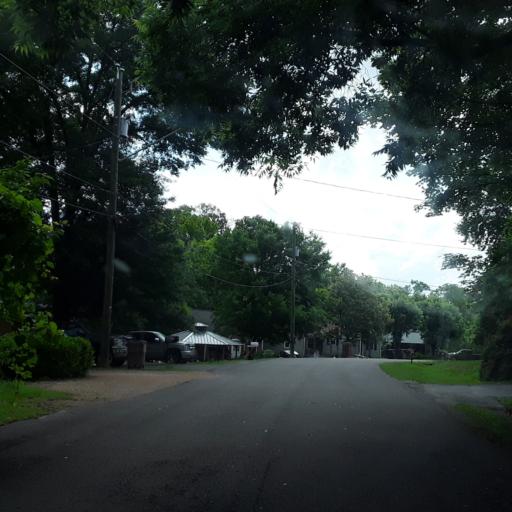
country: US
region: Tennessee
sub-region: Davidson County
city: Oak Hill
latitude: 36.1126
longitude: -86.7286
